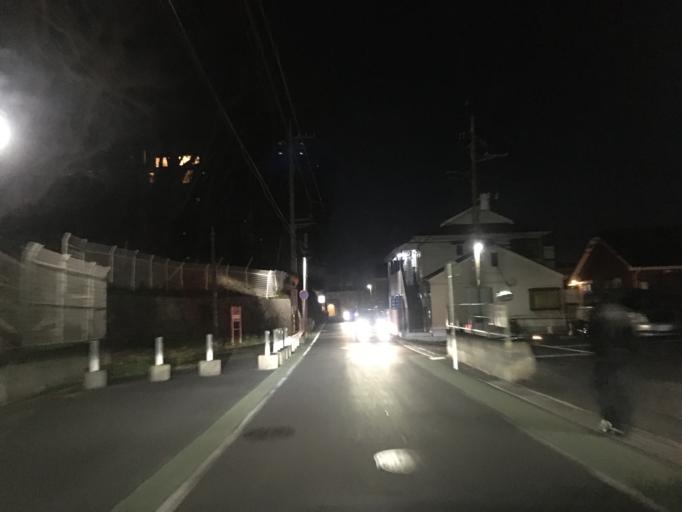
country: JP
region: Tokyo
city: Chofugaoka
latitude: 35.6063
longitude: 139.5206
